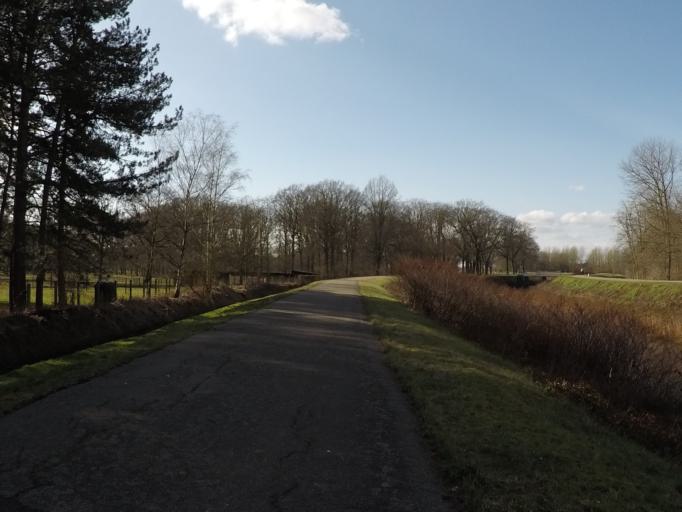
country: BE
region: Flanders
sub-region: Provincie Antwerpen
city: Grobbendonk
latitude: 51.1773
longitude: 4.7153
